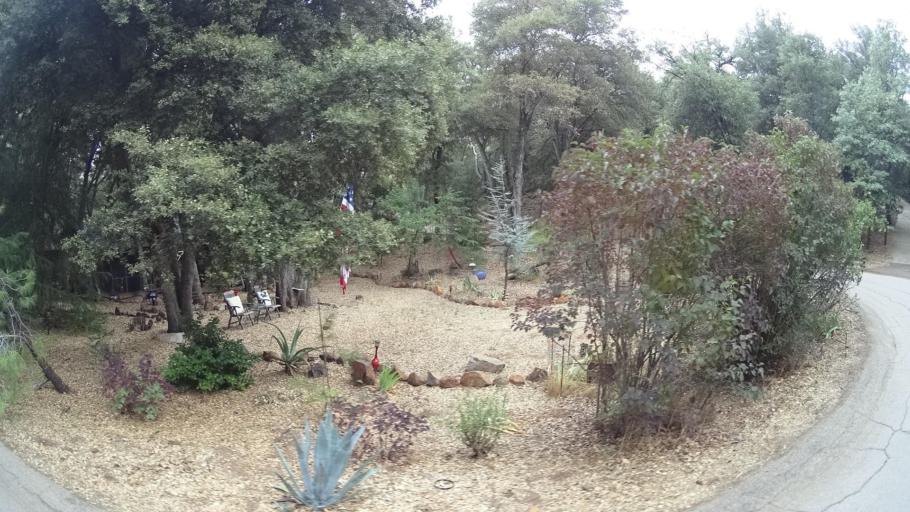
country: US
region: California
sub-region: San Diego County
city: Julian
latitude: 33.0477
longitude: -116.6260
